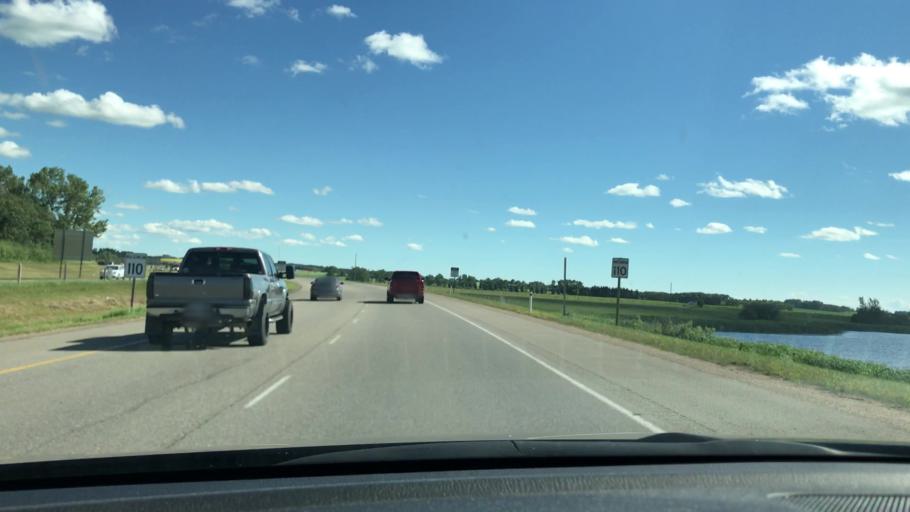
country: CA
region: Alberta
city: Penhold
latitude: 52.1895
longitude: -113.8195
